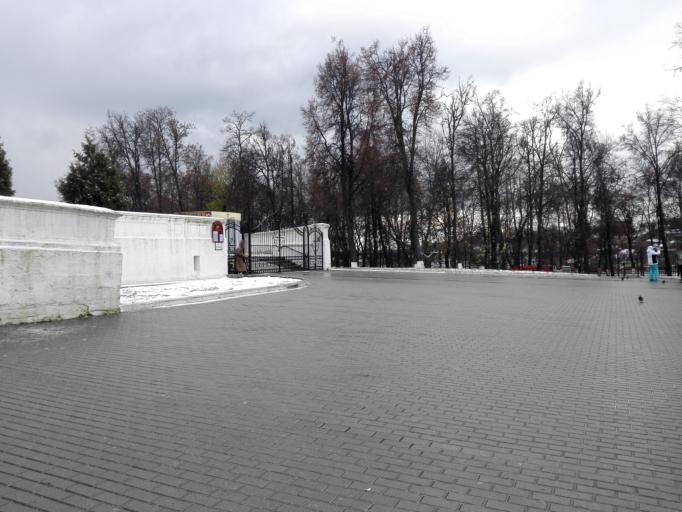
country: RU
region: Vladimir
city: Vladimir
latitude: 56.1279
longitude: 40.4089
